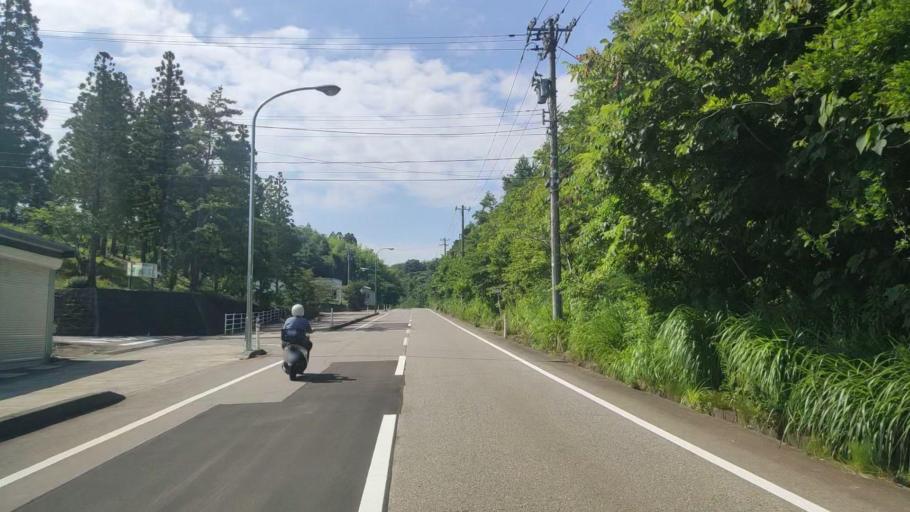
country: JP
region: Ishikawa
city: Komatsu
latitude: 36.3861
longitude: 136.4957
